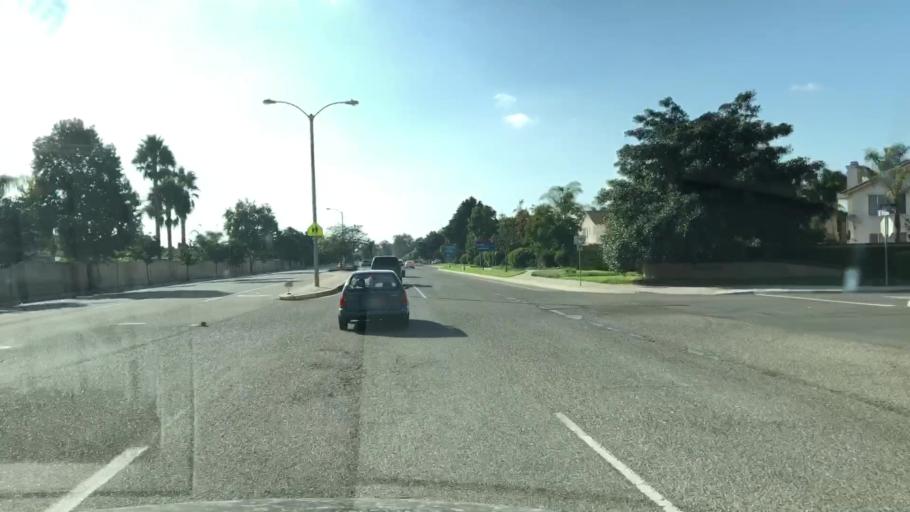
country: US
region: California
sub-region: Ventura County
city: El Rio
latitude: 34.2294
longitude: -119.1916
